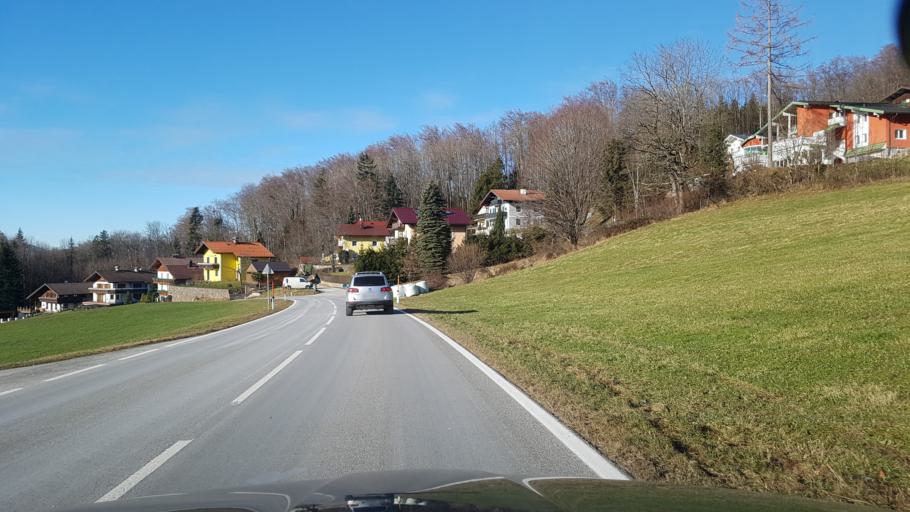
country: AT
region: Salzburg
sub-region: Politischer Bezirk Salzburg-Umgebung
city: Elsbethen
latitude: 47.7707
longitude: 13.1042
